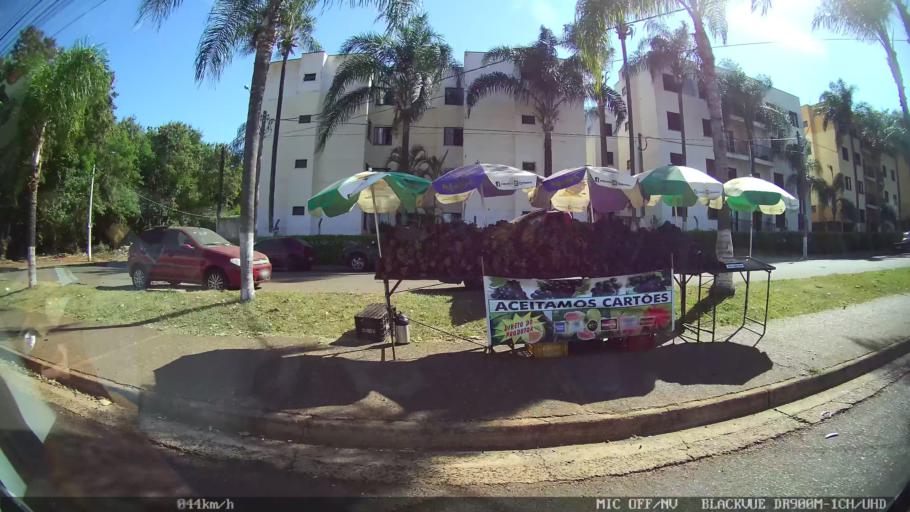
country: BR
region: Sao Paulo
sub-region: Batatais
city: Batatais
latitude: -20.8889
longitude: -47.5780
